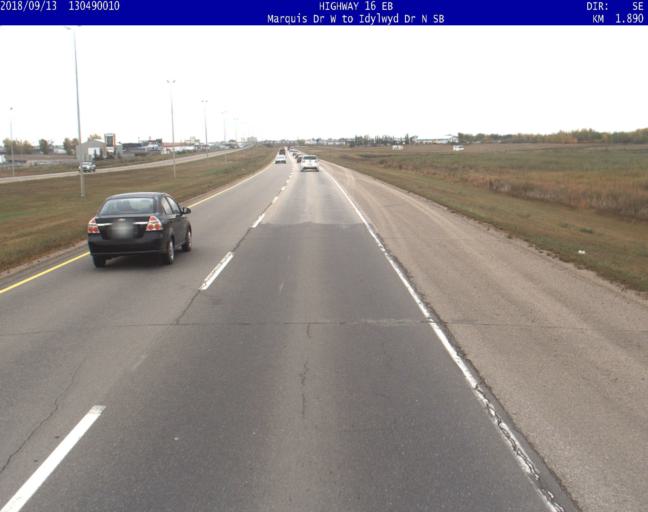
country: CA
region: Saskatchewan
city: Saskatoon
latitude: 52.1900
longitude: -106.6855
